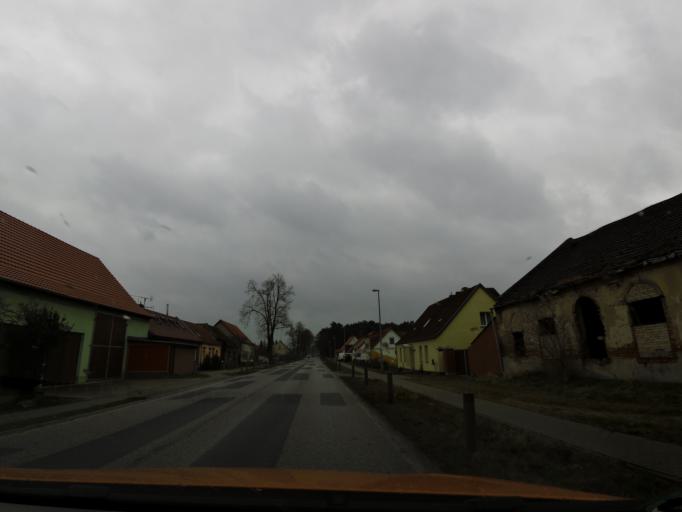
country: DE
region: Brandenburg
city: Ziesar
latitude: 52.2817
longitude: 12.3266
